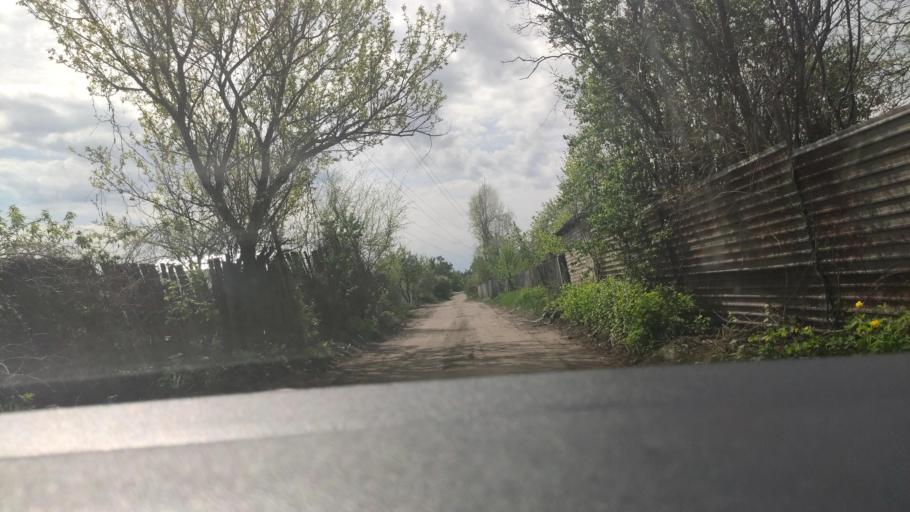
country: RU
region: Voronezj
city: Maslovka
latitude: 51.6063
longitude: 39.2863
